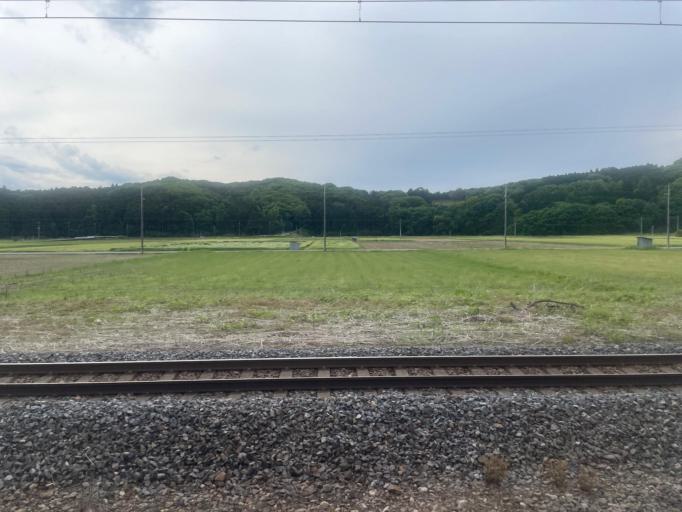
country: JP
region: Tochigi
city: Kanuma
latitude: 36.5064
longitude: 139.7453
